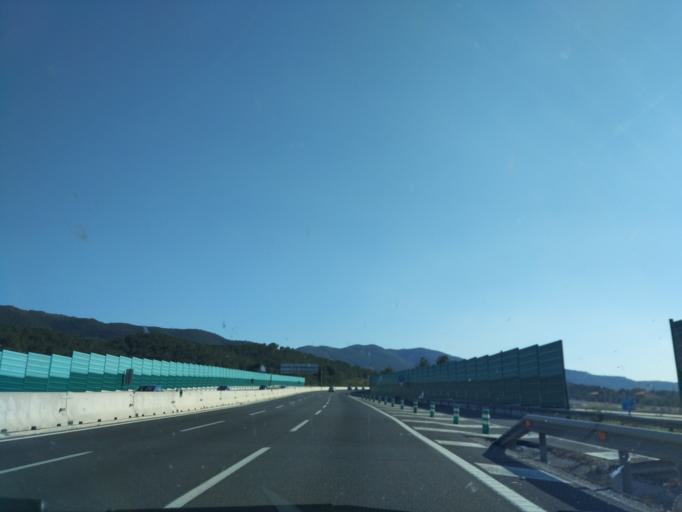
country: ES
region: Murcia
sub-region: Murcia
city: Murcia
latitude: 37.9340
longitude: -1.1540
